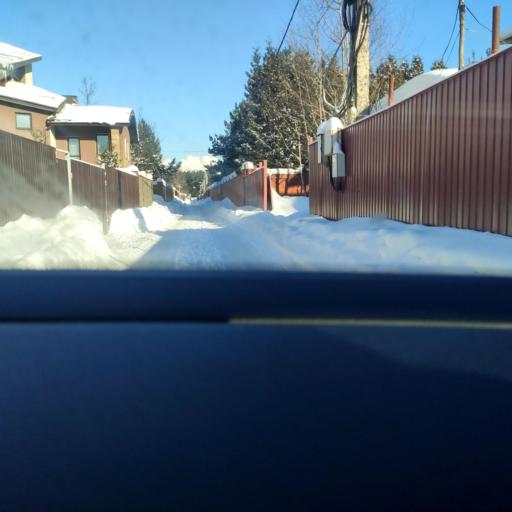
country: RU
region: Moskovskaya
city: Mosrentgen
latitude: 55.6293
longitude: 37.4610
